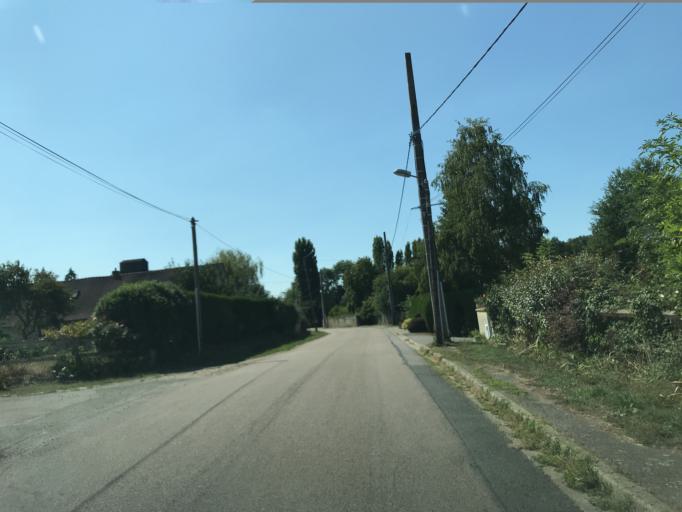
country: FR
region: Haute-Normandie
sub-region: Departement de l'Eure
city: Houlbec-Cocherel
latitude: 49.0929
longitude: 1.3347
